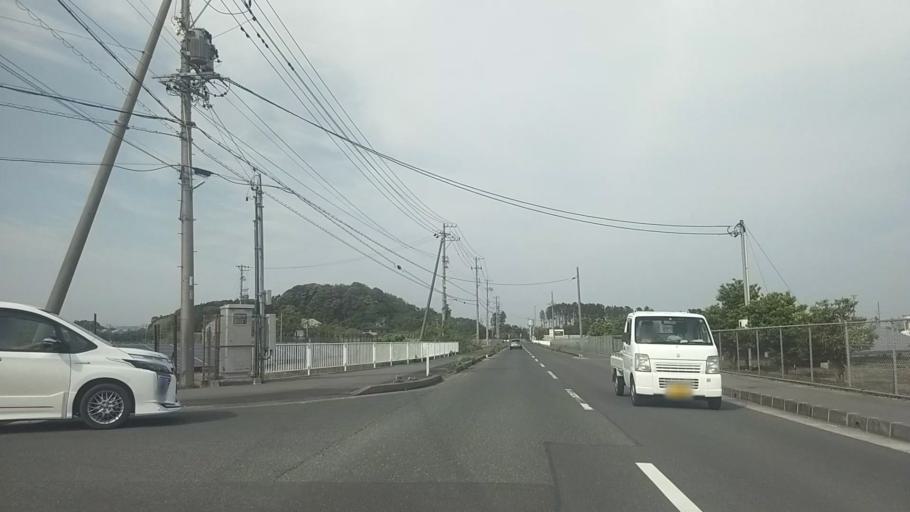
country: JP
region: Shizuoka
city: Kosai-shi
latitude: 34.7238
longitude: 137.6009
